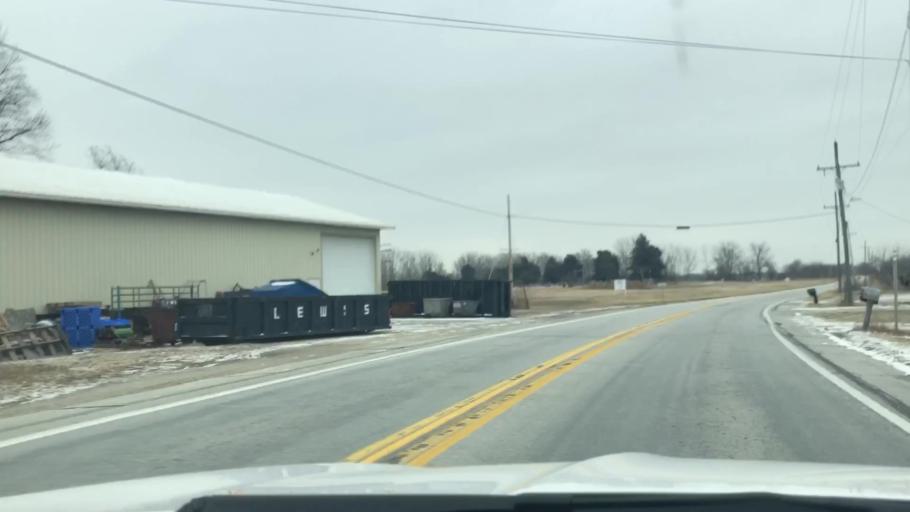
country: US
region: Indiana
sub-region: Fulton County
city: Rochester
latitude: 41.0542
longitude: -86.1238
